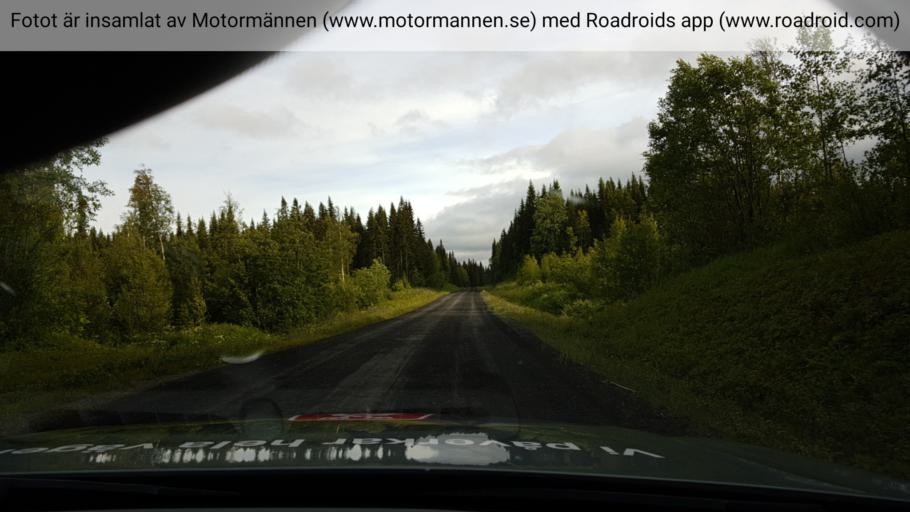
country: SE
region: Jaemtland
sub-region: OEstersunds Kommun
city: Lit
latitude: 63.6440
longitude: 15.0746
